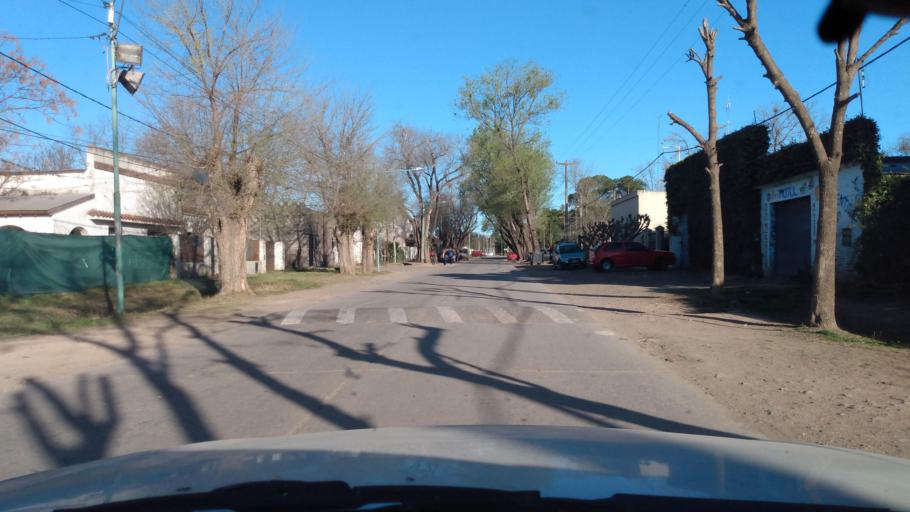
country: AR
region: Buenos Aires
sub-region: Partido de Lujan
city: Lujan
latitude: -34.6251
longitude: -59.2539
